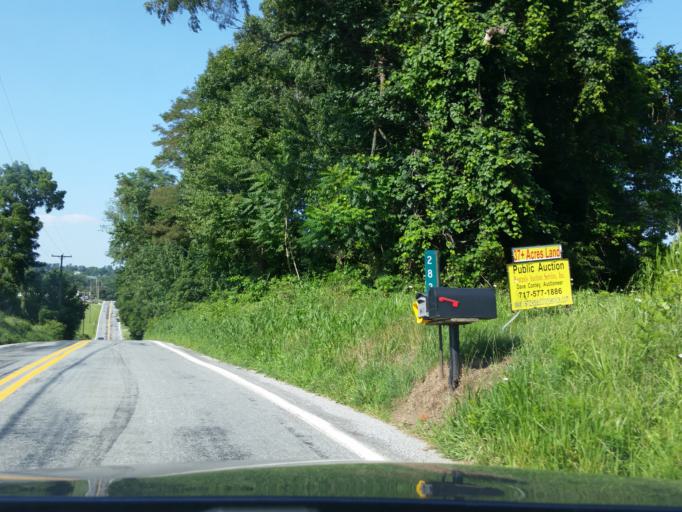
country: US
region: Pennsylvania
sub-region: York County
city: Hallam
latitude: 40.0188
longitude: -76.5904
